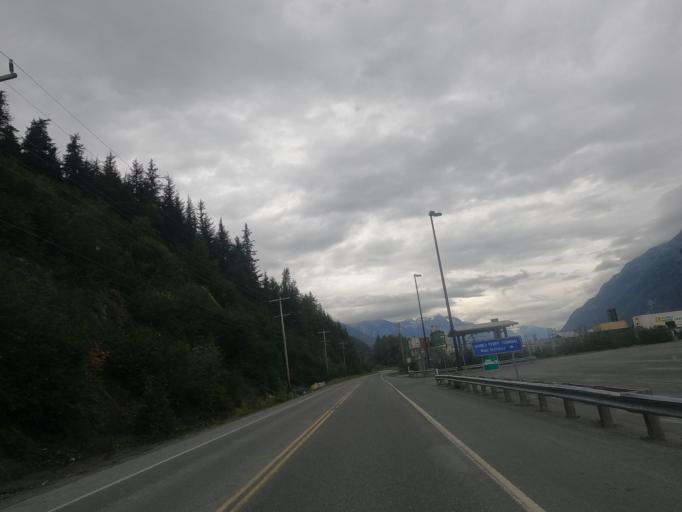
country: US
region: Alaska
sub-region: Haines Borough
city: Haines
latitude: 59.2816
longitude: -135.4657
